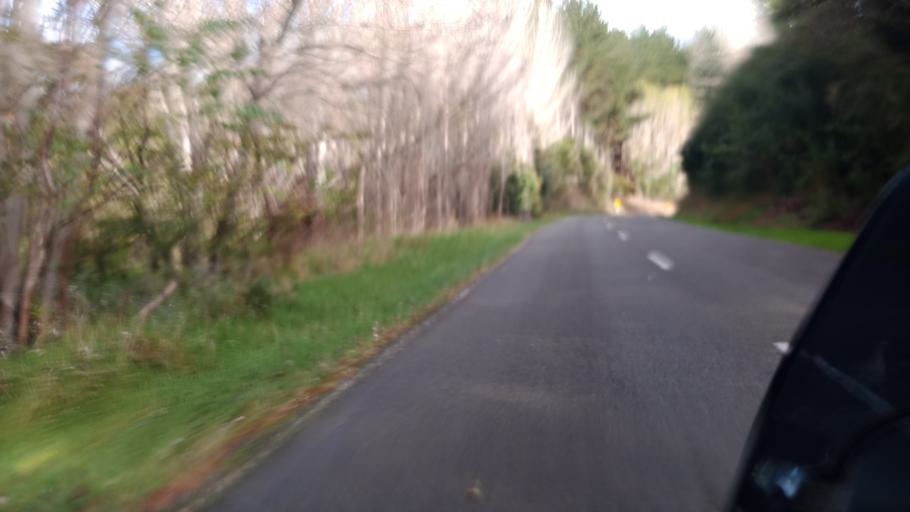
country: NZ
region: Gisborne
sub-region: Gisborne District
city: Gisborne
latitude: -38.5620
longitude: 177.7126
